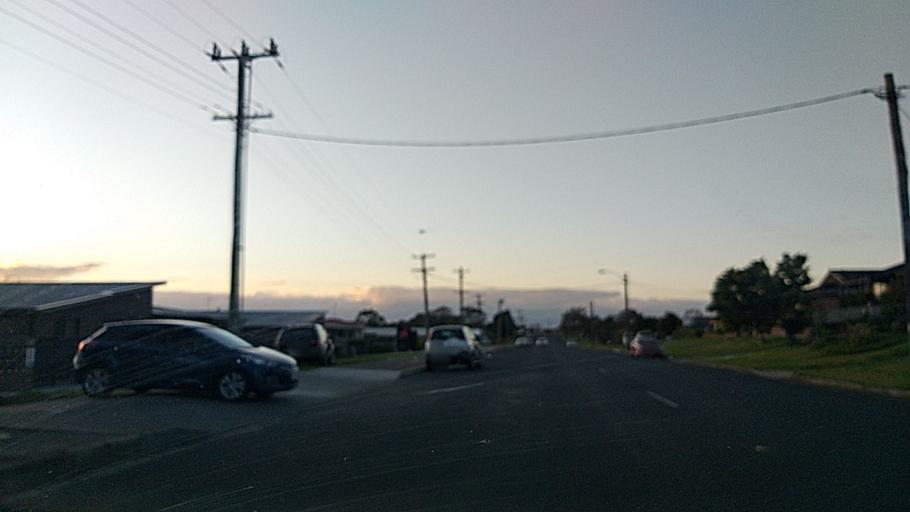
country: AU
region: New South Wales
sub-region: Wollongong
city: Koonawarra
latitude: -34.4970
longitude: 150.8205
